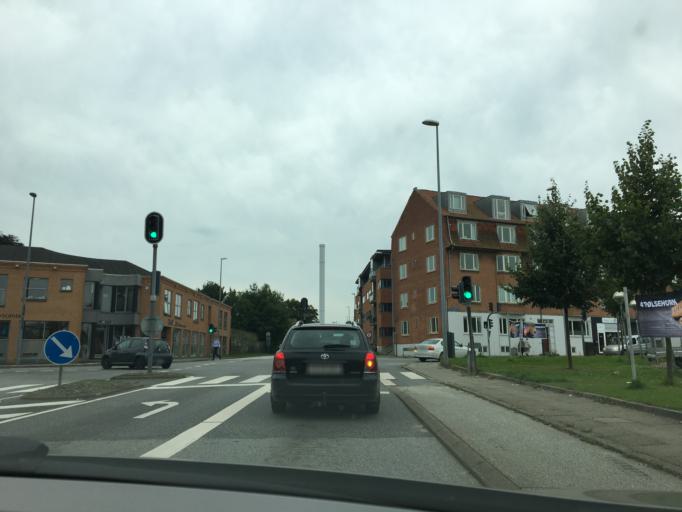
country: DK
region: Central Jutland
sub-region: Herning Kommune
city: Herning
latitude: 56.1353
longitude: 8.9855
